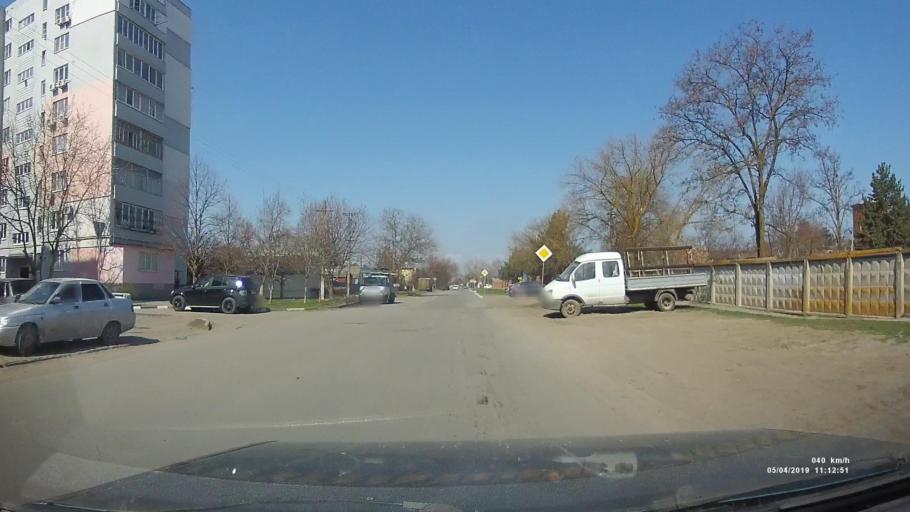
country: RU
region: Rostov
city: Azov
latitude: 47.0997
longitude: 39.4348
